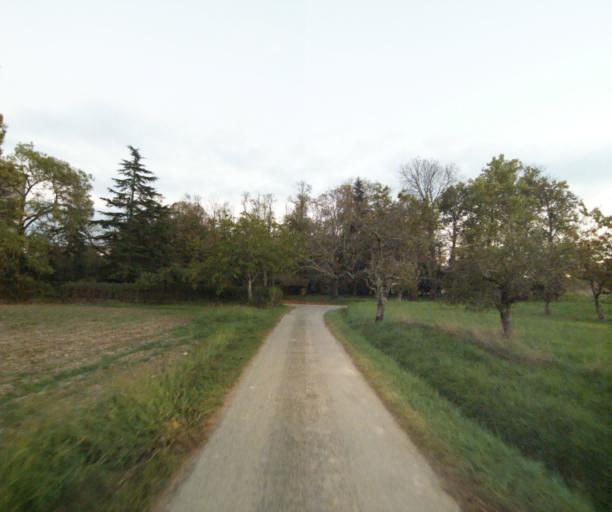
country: FR
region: Midi-Pyrenees
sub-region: Departement du Gers
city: Vic-Fezensac
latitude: 43.8085
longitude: 0.2554
